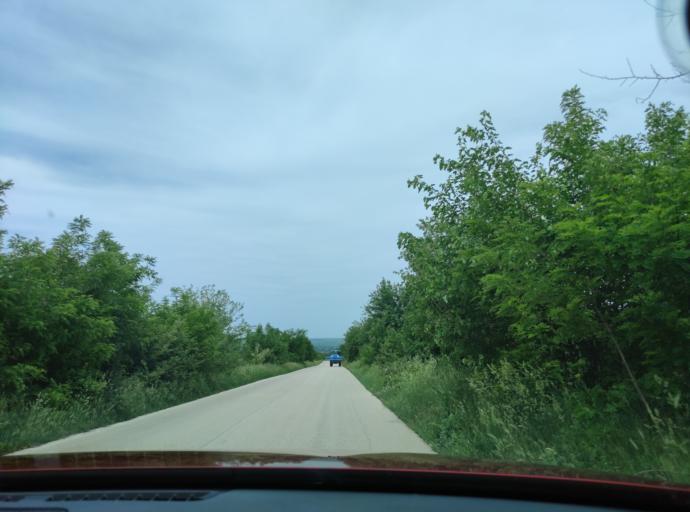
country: BG
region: Pleven
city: Iskur
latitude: 43.5299
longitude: 24.3072
